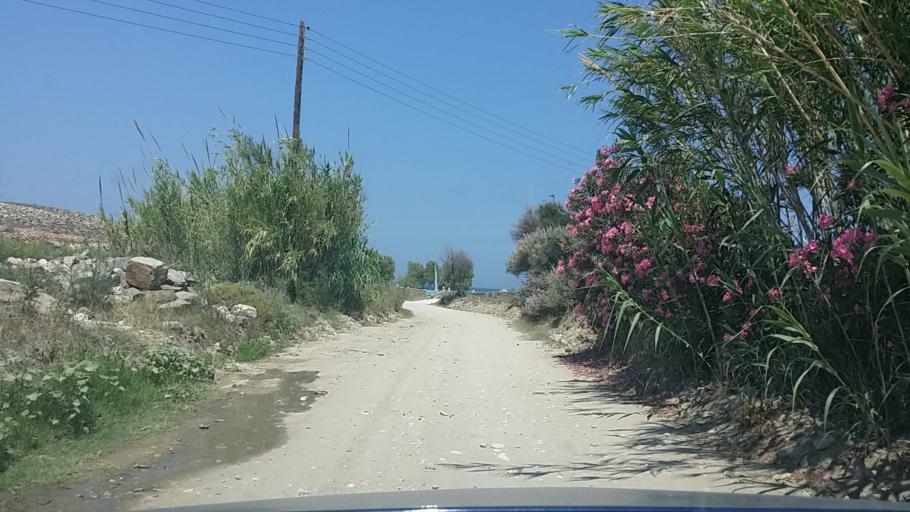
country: GR
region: South Aegean
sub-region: Nomos Kykladon
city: Paros
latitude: 37.0699
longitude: 25.1288
